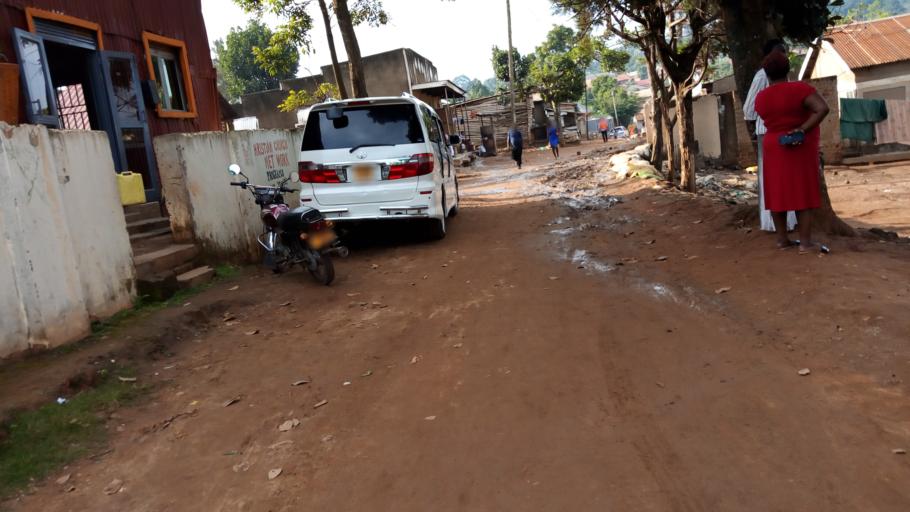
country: UG
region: Central Region
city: Kampala Central Division
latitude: 0.3737
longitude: 32.5524
